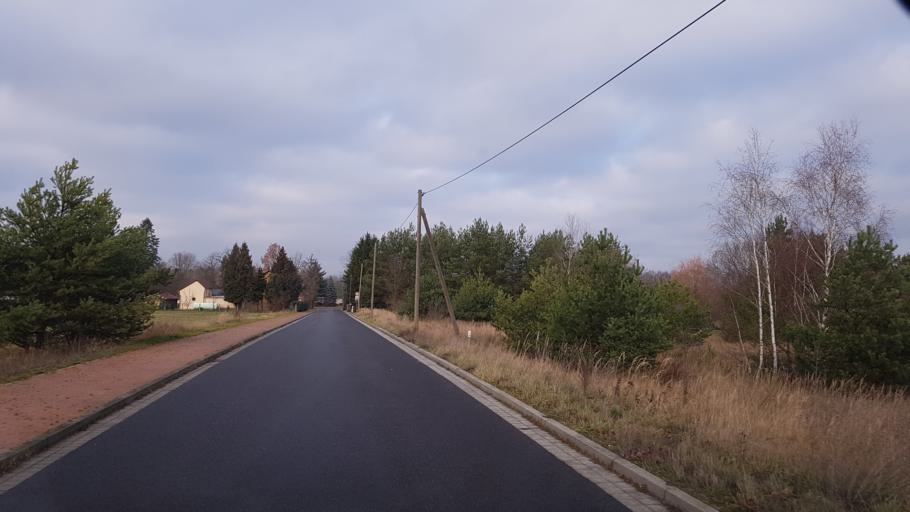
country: DE
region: Brandenburg
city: Sallgast
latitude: 51.5915
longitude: 13.8124
